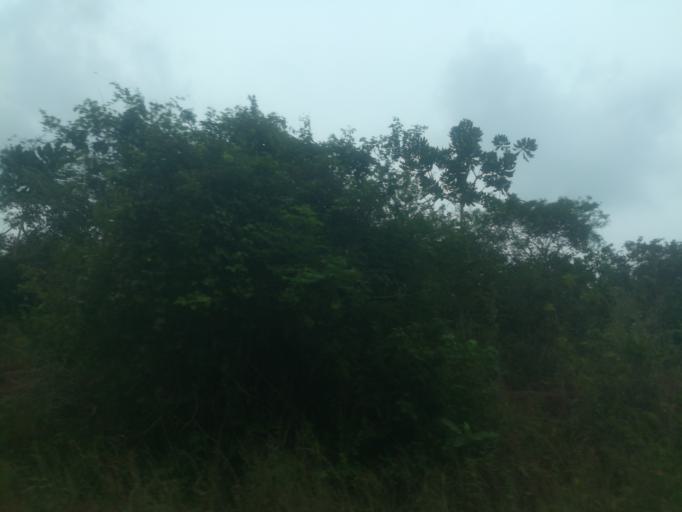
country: NG
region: Ogun
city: Ayetoro
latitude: 7.1011
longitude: 3.1324
